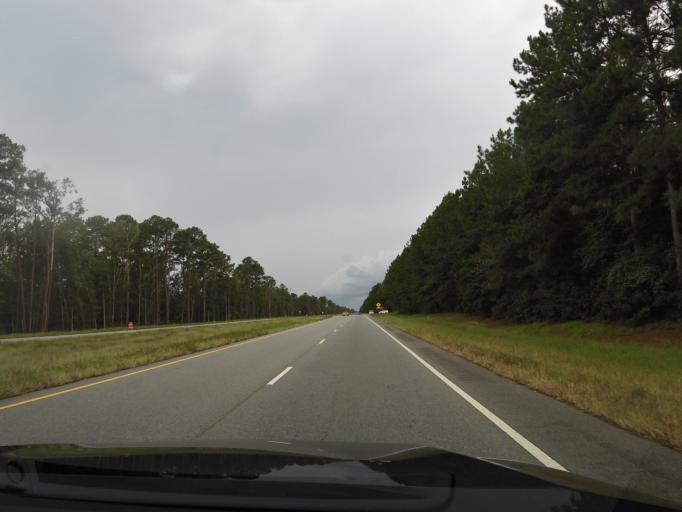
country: US
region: Georgia
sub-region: Glynn County
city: Dock Junction
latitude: 31.3344
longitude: -81.5969
